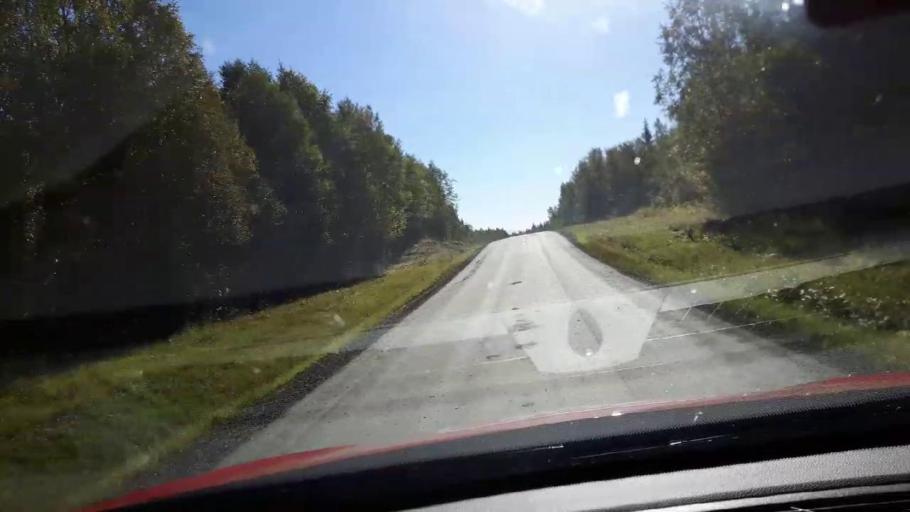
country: NO
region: Nord-Trondelag
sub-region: Lierne
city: Sandvika
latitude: 64.6037
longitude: 13.9666
